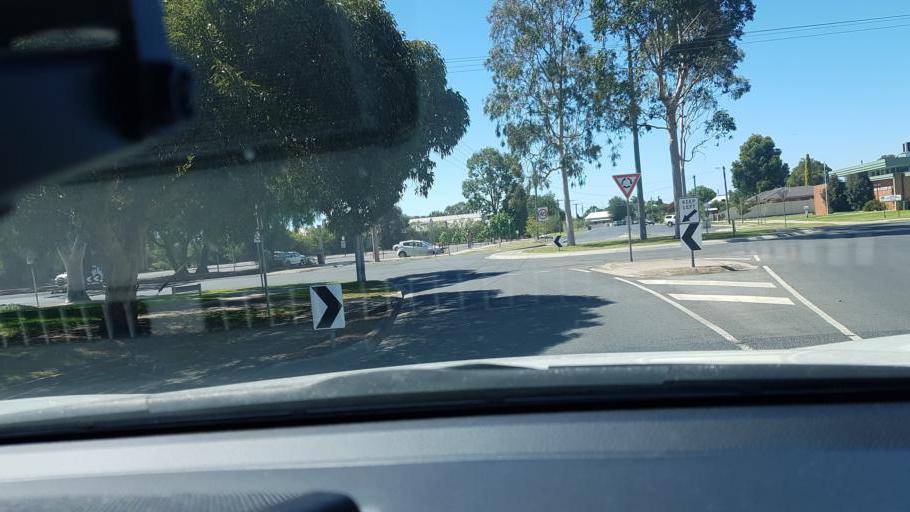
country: AU
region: Victoria
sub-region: Horsham
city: Horsham
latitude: -36.7142
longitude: 142.2015
